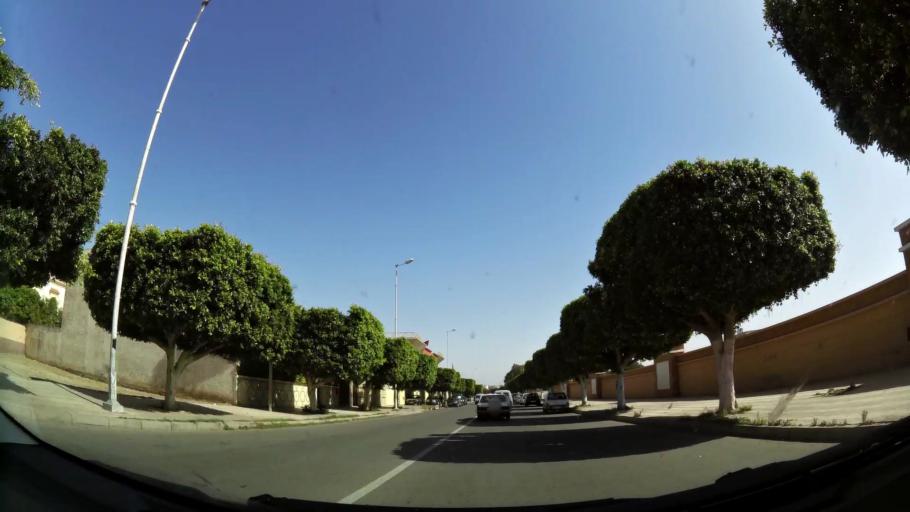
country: MA
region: Souss-Massa-Draa
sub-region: Inezgane-Ait Mellou
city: Inezgane
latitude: 30.3632
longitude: -9.5438
